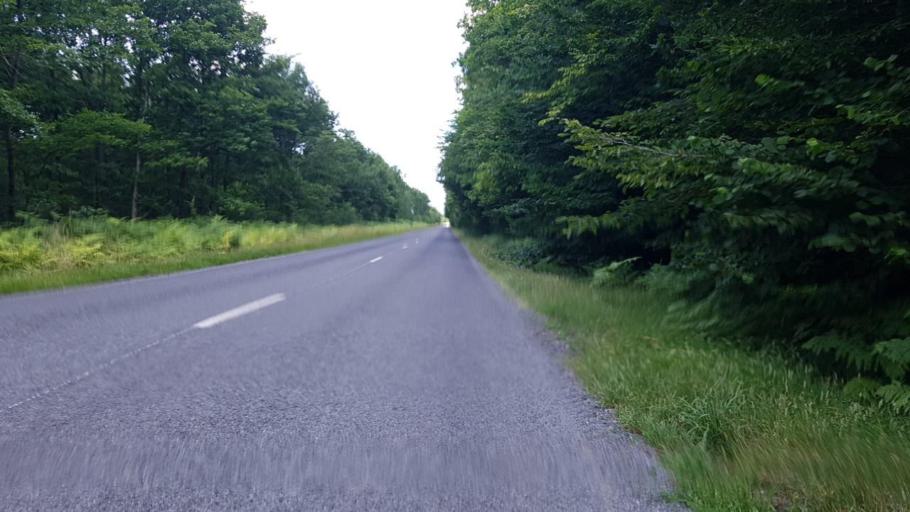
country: FR
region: Picardie
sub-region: Departement de l'Oise
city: Carlepont
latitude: 49.5154
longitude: 2.9834
